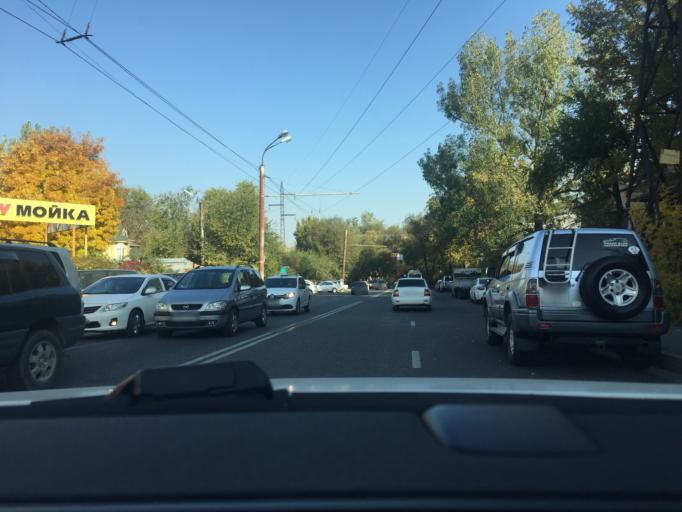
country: KZ
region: Almaty Qalasy
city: Almaty
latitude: 43.2440
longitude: 76.9081
